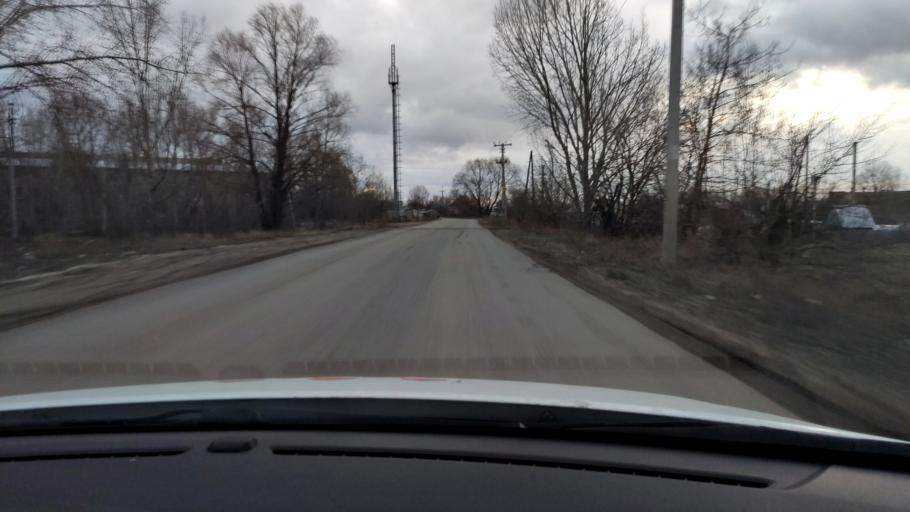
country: RU
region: Tatarstan
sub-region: Gorod Kazan'
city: Kazan
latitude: 55.7226
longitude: 49.0942
